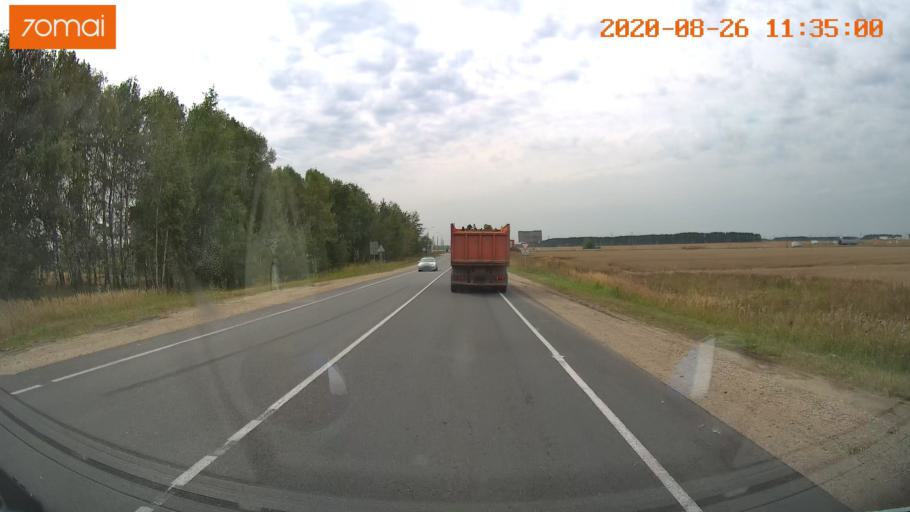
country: RU
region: Rjazan
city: Shilovo
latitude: 54.2790
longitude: 40.8380
